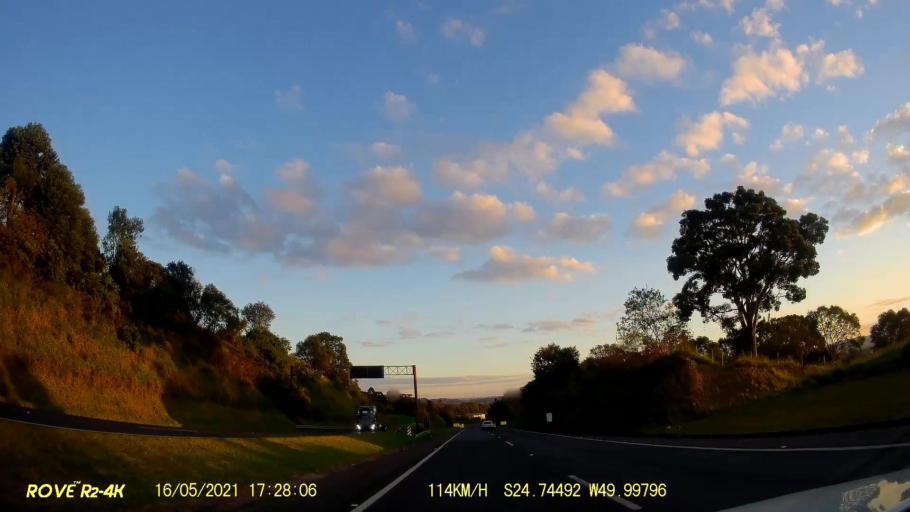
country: BR
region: Parana
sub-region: Castro
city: Castro
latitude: -24.7454
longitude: -49.9984
